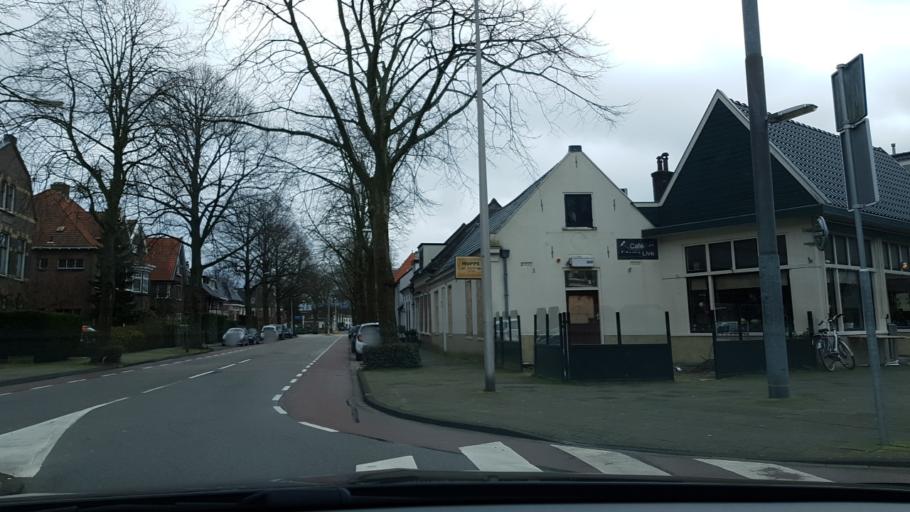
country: NL
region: North Holland
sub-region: Gemeente Heemstede
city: Heemstede
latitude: 52.3455
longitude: 4.6204
